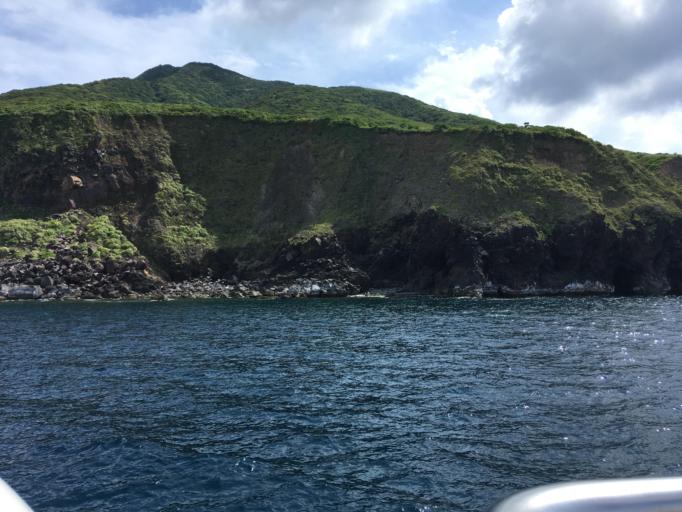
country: TW
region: Taiwan
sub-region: Yilan
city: Yilan
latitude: 24.8516
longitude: 121.9537
